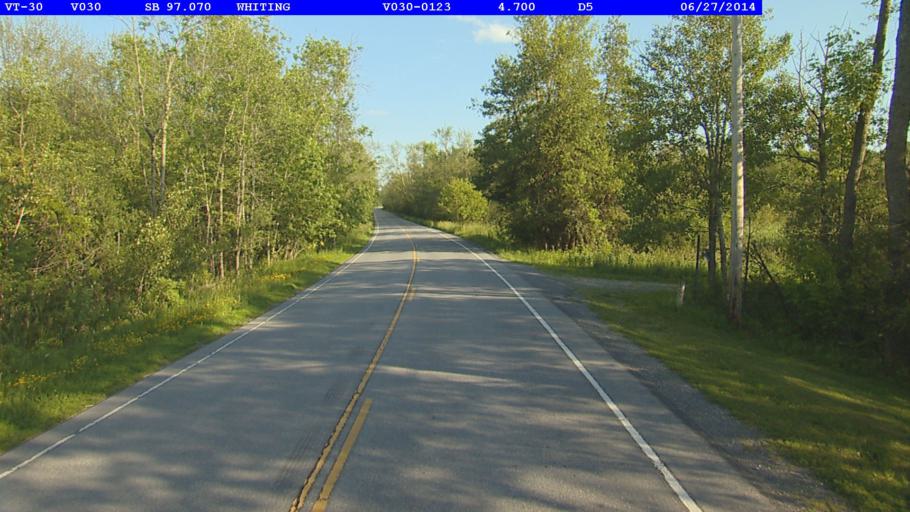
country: US
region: Vermont
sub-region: Addison County
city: Middlebury (village)
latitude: 43.9044
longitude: -73.2079
